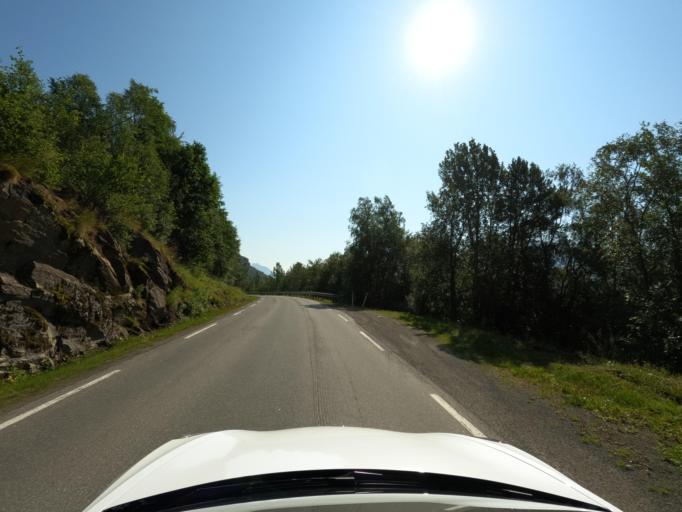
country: NO
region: Nordland
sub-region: Narvik
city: Narvik
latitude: 68.3554
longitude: 17.2726
